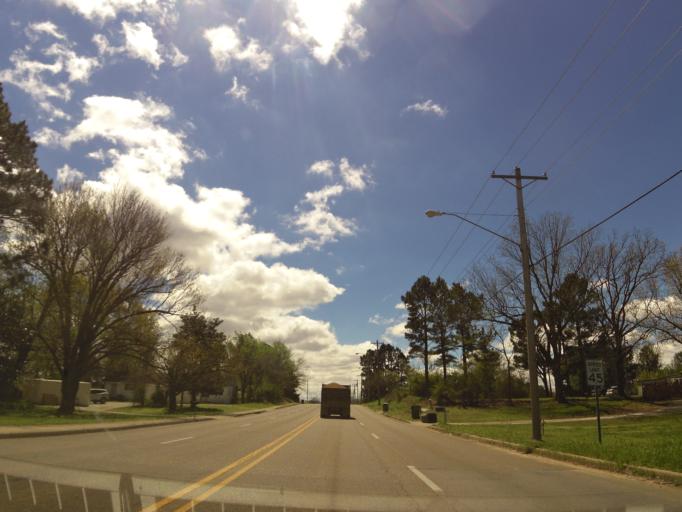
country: US
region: Arkansas
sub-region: Craighead County
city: Jonesboro
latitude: 35.8699
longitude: -90.7029
